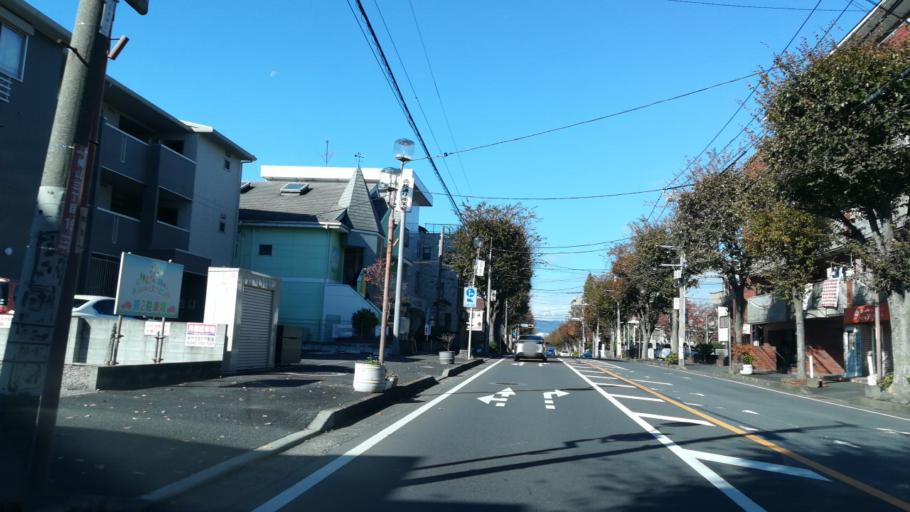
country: JP
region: Kanagawa
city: Zama
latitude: 35.5664
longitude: 139.3669
